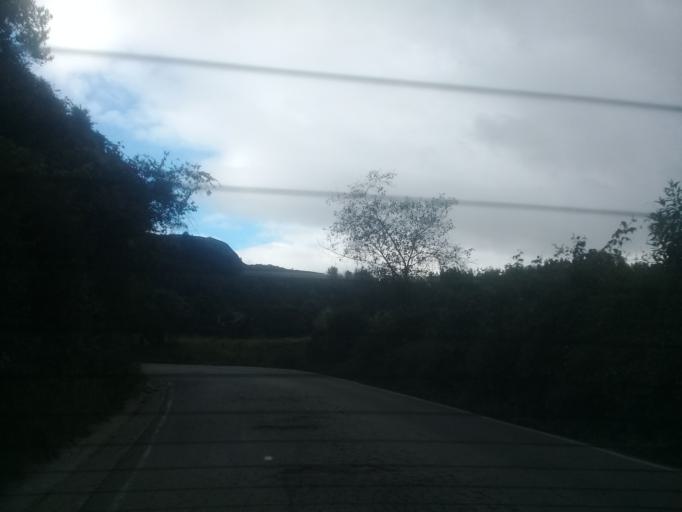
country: CO
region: Cundinamarca
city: Tabio
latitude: 4.9451
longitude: -74.1075
